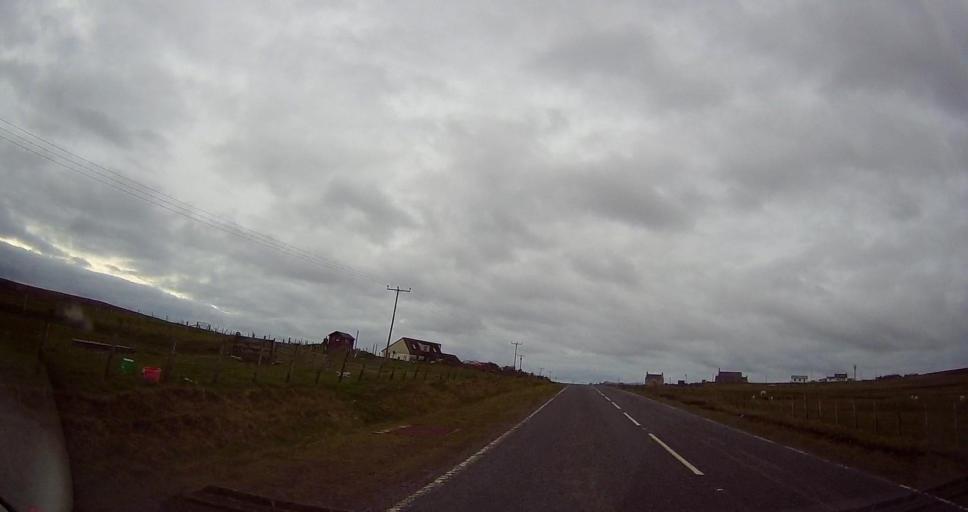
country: GB
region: Scotland
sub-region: Shetland Islands
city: Shetland
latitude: 60.6628
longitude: -1.0529
